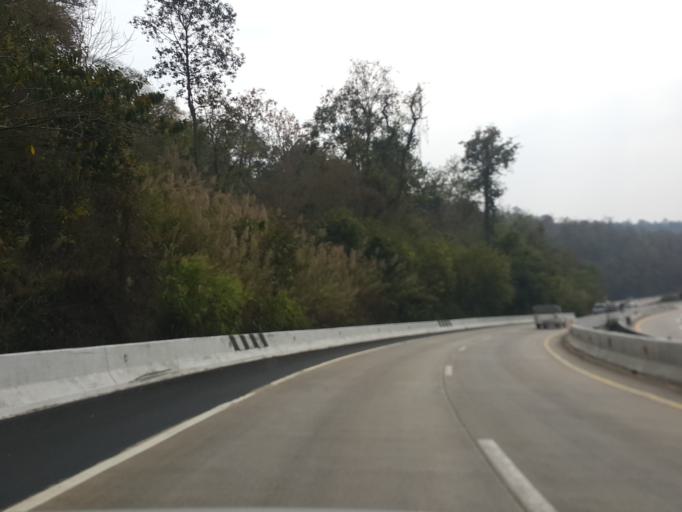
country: TH
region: Lampang
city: Hang Chat
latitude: 18.3779
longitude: 99.2318
